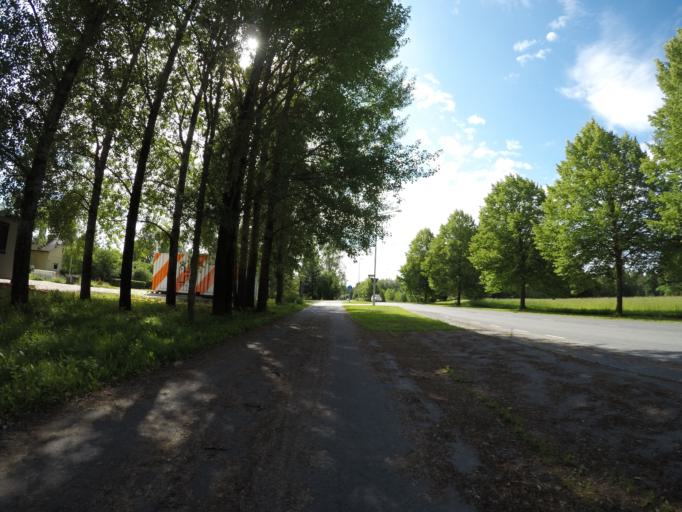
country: FI
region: Haeme
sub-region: Haemeenlinna
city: Haemeenlinna
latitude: 60.9902
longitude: 24.4044
